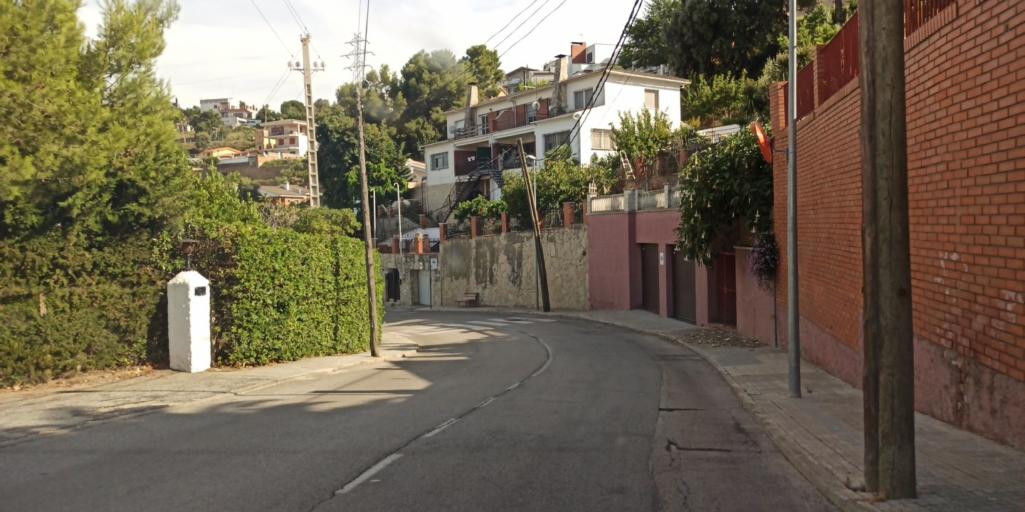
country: ES
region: Catalonia
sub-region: Provincia de Barcelona
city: Santa Coloma de Cervello
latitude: 41.3592
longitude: 2.0036
